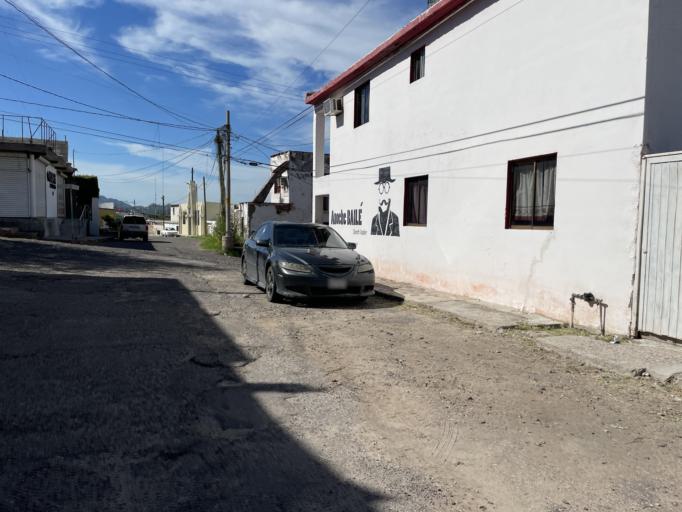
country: MX
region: Sonora
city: Hermosillo
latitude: 29.0732
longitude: -110.9544
